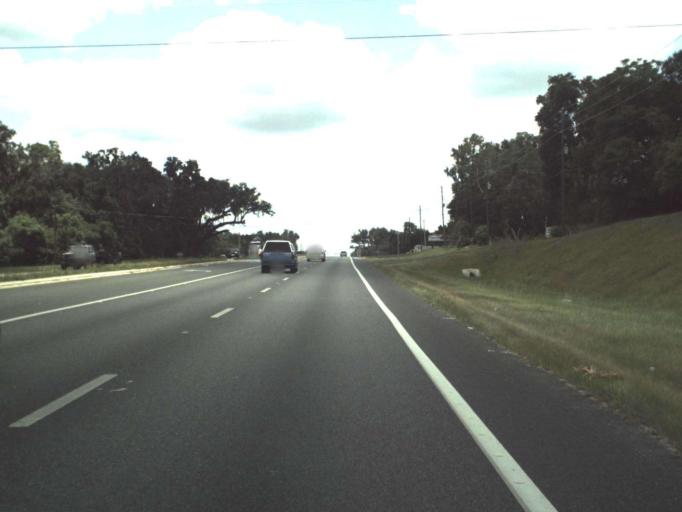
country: US
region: Florida
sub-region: Sumter County
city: Wildwood
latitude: 28.8938
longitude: -82.0369
